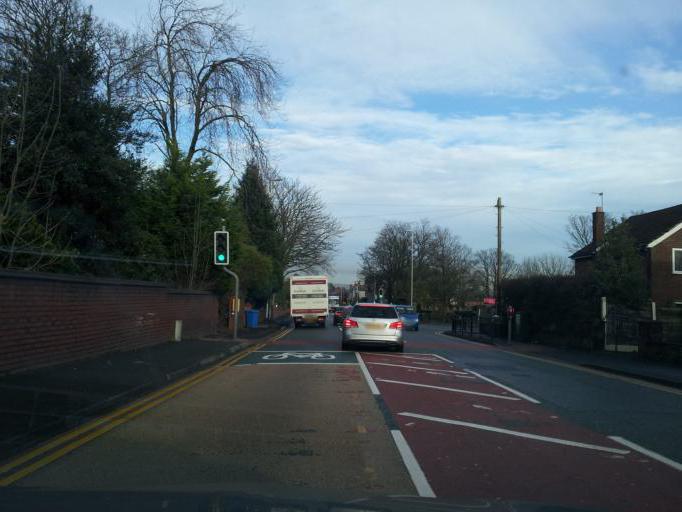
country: GB
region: England
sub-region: Manchester
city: Heywood
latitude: 53.5822
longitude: -2.2120
